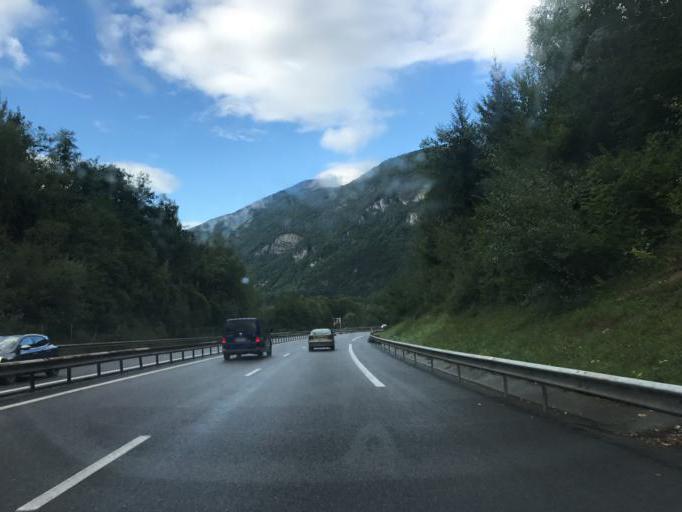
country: FR
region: Rhone-Alpes
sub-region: Departement de la Savoie
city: Novalaise
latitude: 45.5752
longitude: 5.7921
